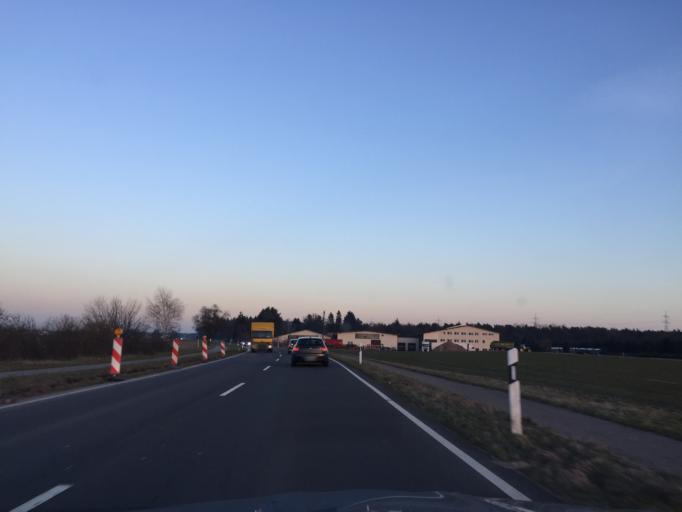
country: DE
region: Baden-Wuerttemberg
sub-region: Karlsruhe Region
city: Neulussheim
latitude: 49.2894
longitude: 8.5370
